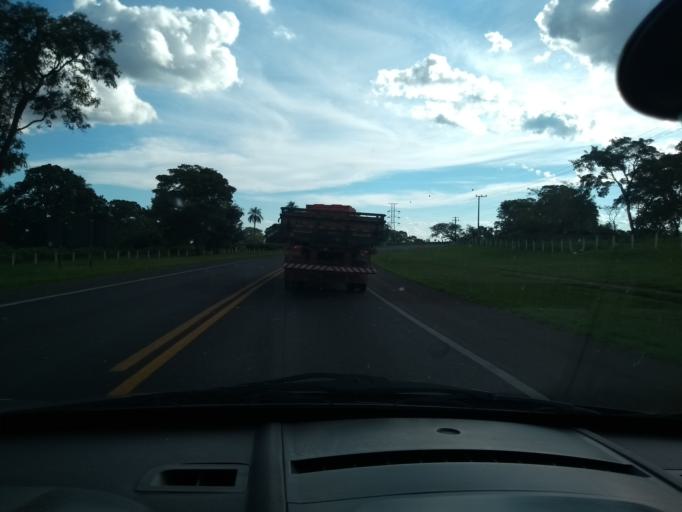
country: BR
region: Sao Paulo
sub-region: Casa Branca
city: Casa Branca
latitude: -21.7970
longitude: -47.0755
